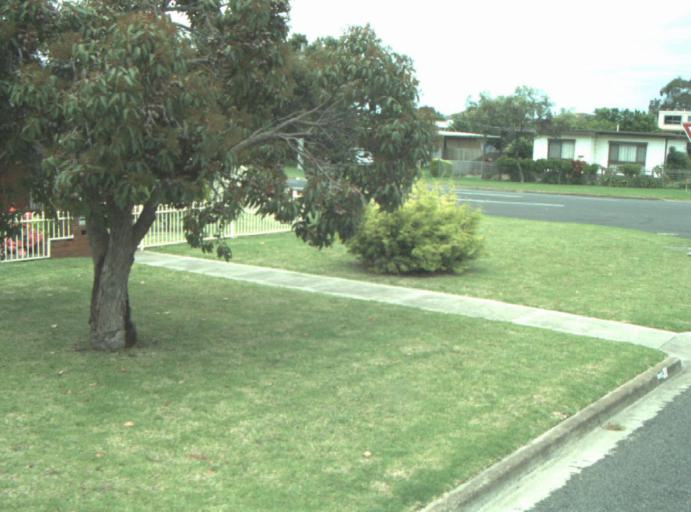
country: AU
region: Victoria
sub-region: Greater Geelong
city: Clifton Springs
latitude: -38.1158
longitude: 144.6620
